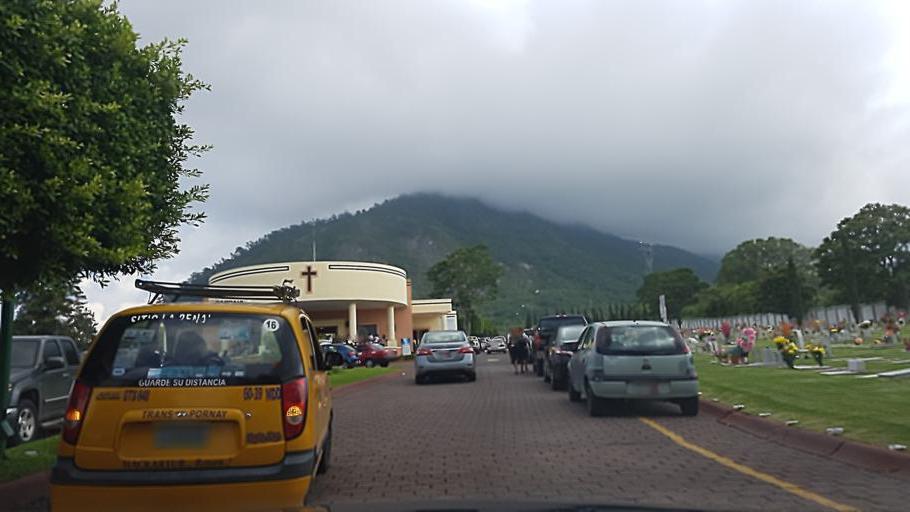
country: MX
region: Nayarit
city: Tepic
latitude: 21.5216
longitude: -104.9298
